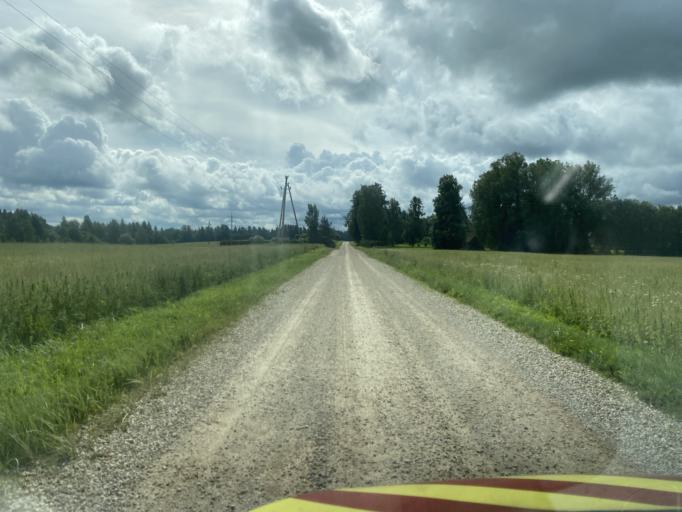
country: EE
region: Viljandimaa
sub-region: Karksi vald
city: Karksi-Nuia
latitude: 58.0664
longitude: 25.5262
